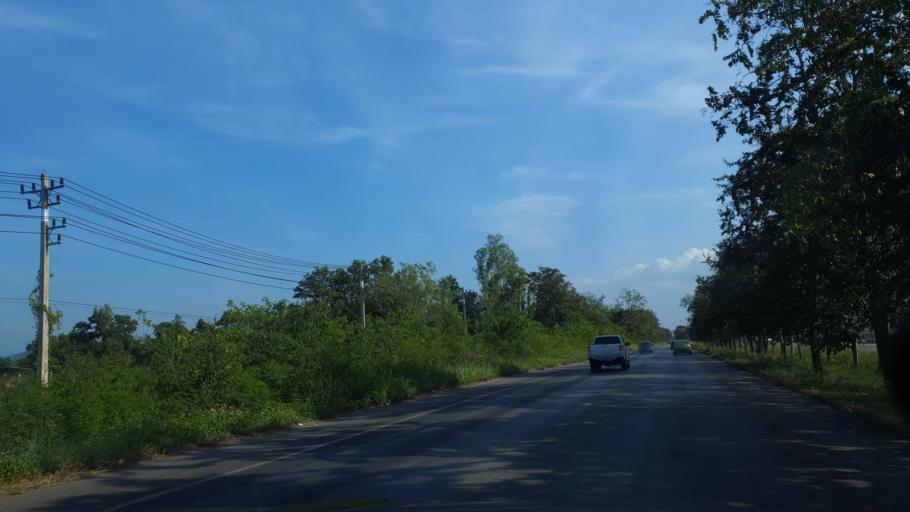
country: TH
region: Surat Thani
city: Phunphin
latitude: 9.0153
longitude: 99.1835
